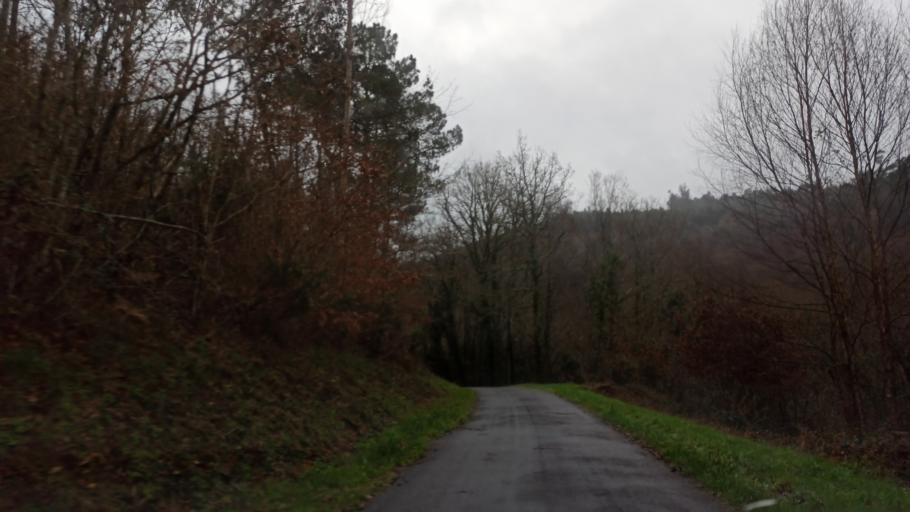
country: ES
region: Galicia
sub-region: Provincia da Coruna
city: Cesuras
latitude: 43.1758
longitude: -8.1676
